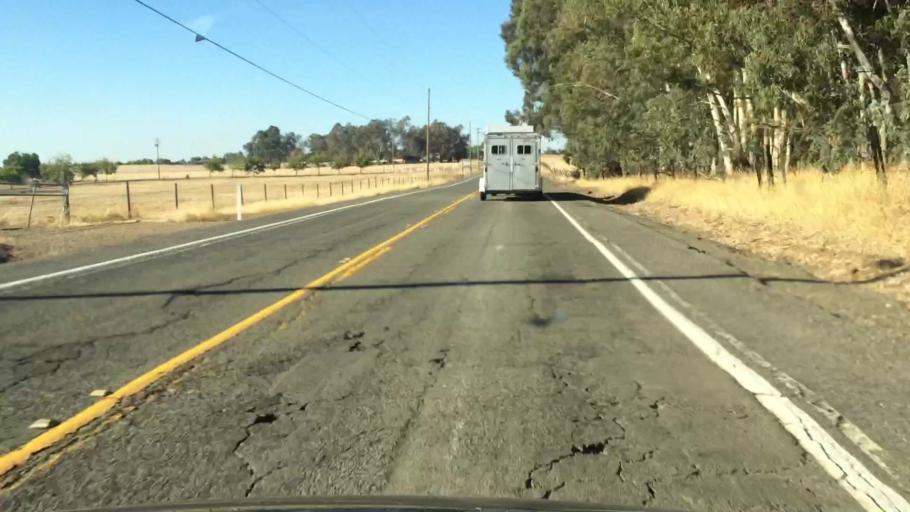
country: US
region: California
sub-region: Sacramento County
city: Clay
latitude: 38.4085
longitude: -121.1739
